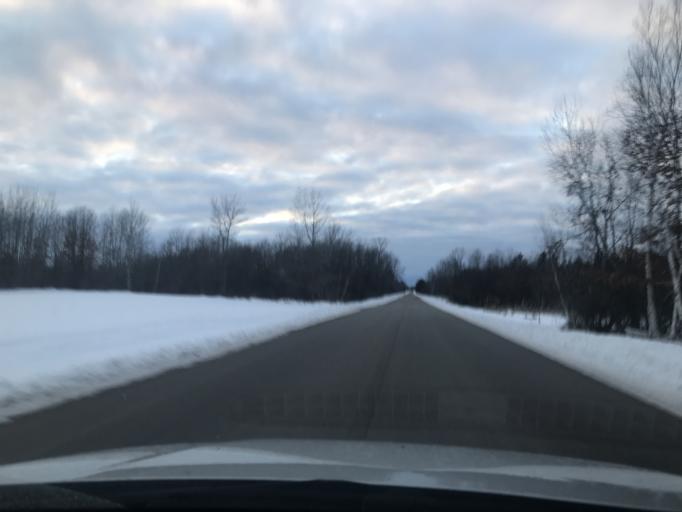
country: US
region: Wisconsin
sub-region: Marinette County
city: Peshtigo
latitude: 45.1646
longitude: -87.7406
